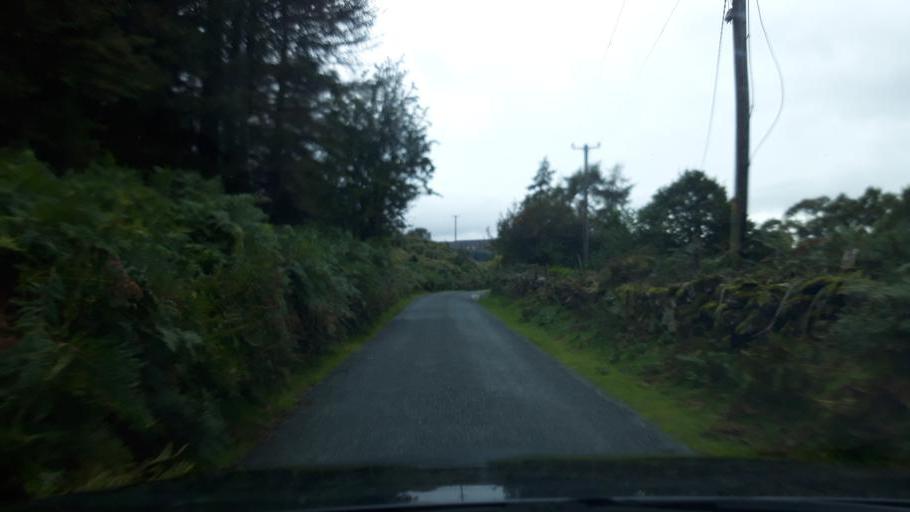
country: IE
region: Leinster
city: Ballinteer
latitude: 53.1801
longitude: -6.2664
